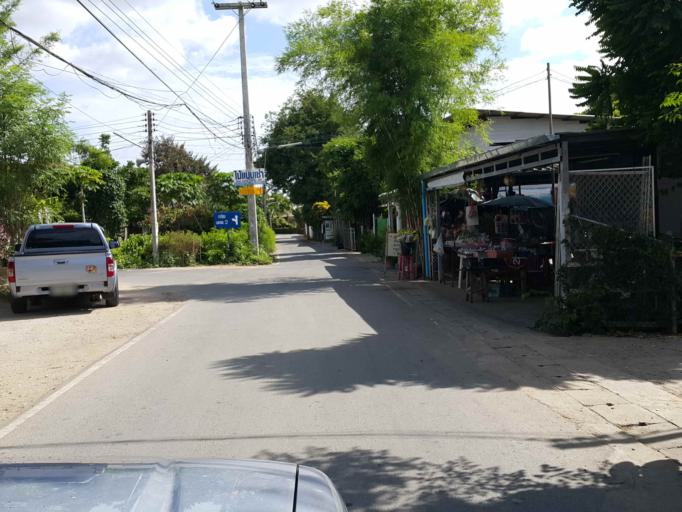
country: TH
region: Chiang Mai
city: Saraphi
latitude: 18.7383
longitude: 98.9983
